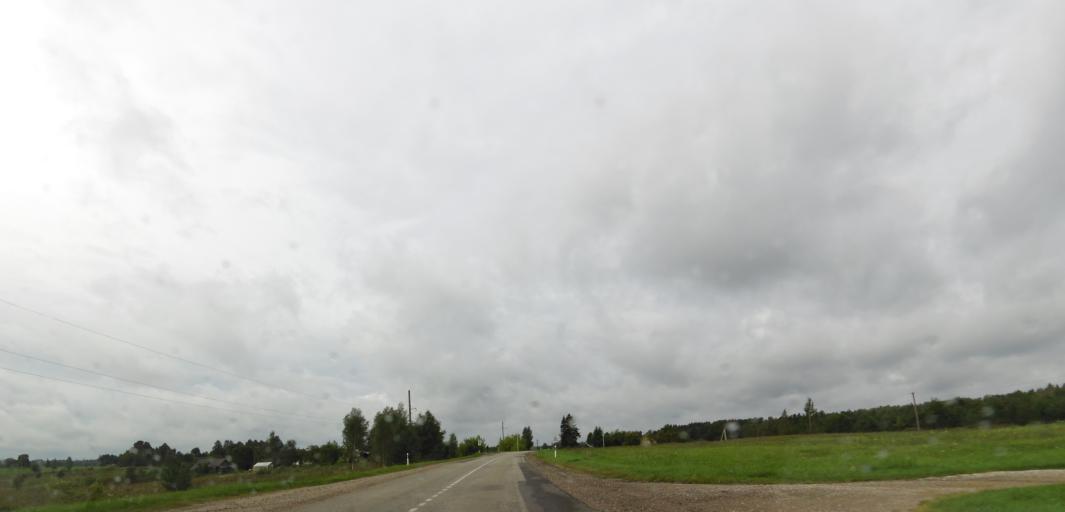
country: LT
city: Moletai
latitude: 55.2113
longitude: 25.3183
